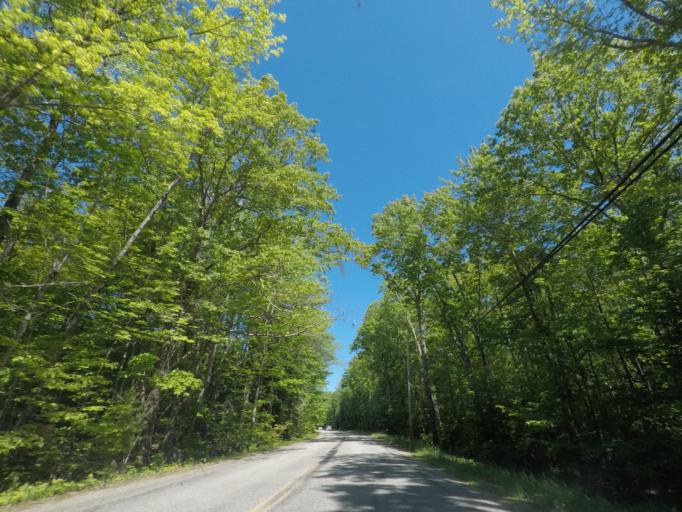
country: US
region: Maine
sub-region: Kennebec County
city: Manchester
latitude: 44.2552
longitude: -69.9022
